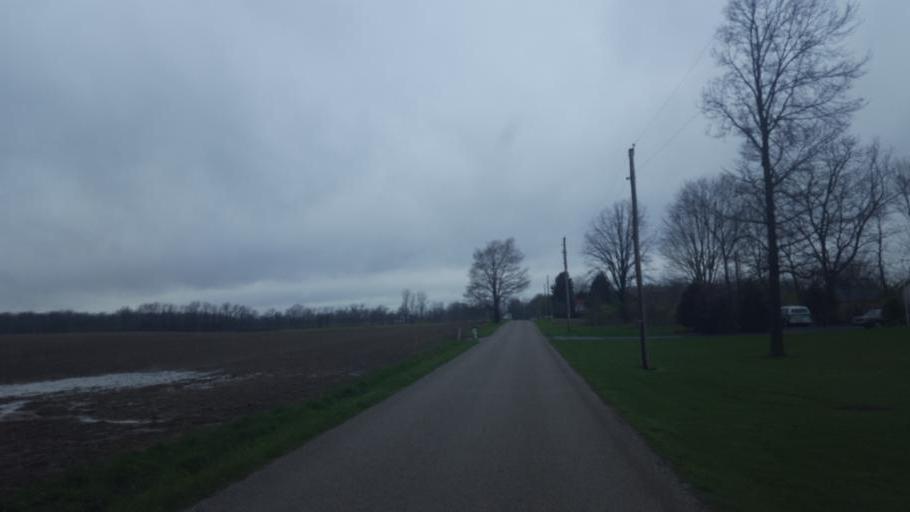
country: US
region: Ohio
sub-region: Morrow County
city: Mount Gilead
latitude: 40.5310
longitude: -82.8603
